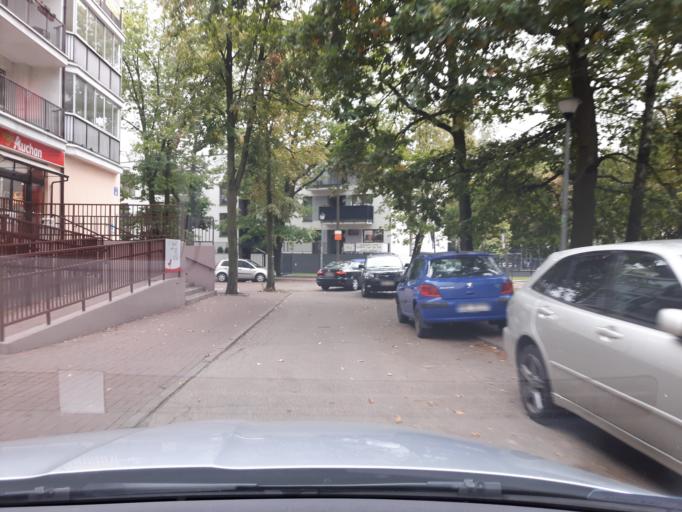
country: PL
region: Masovian Voivodeship
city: Zielonka
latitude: 52.3038
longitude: 21.1639
